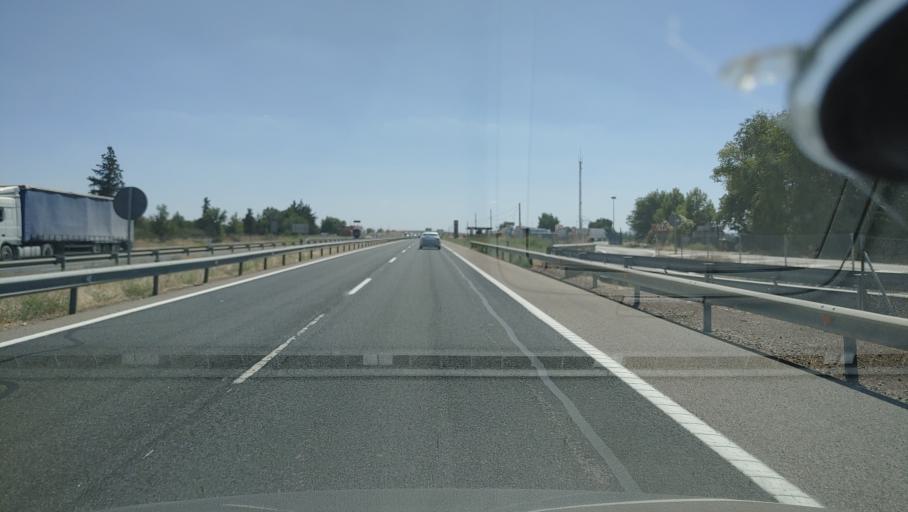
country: ES
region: Castille-La Mancha
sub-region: Provincia de Ciudad Real
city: Manzanares
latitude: 39.1116
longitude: -3.3775
